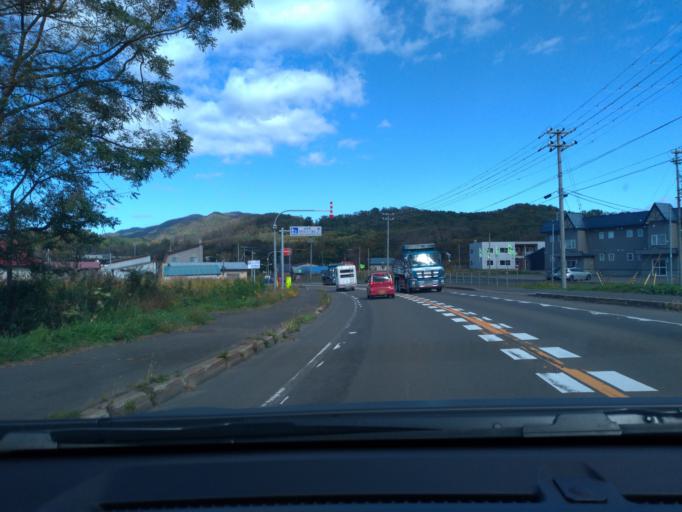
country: JP
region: Hokkaido
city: Ishikari
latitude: 43.3960
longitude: 141.4371
